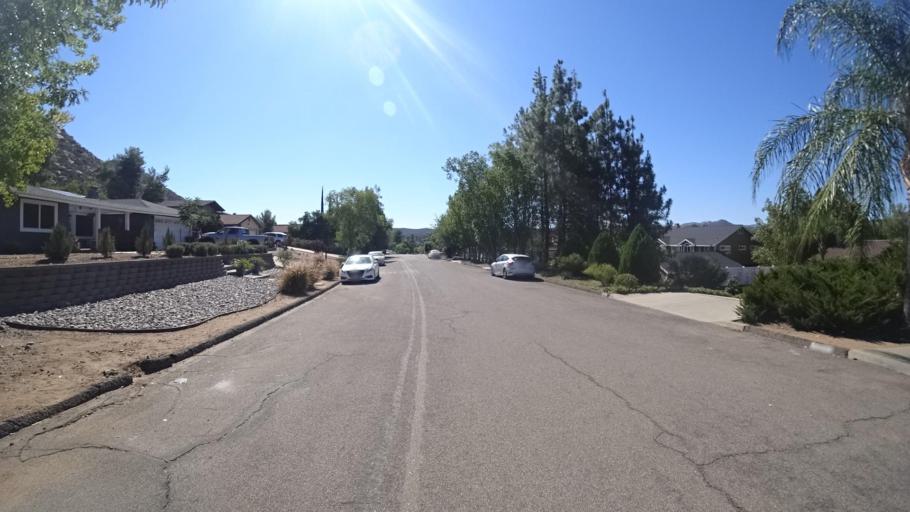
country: US
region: California
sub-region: San Diego County
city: San Diego Country Estates
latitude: 33.0124
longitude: -116.7874
